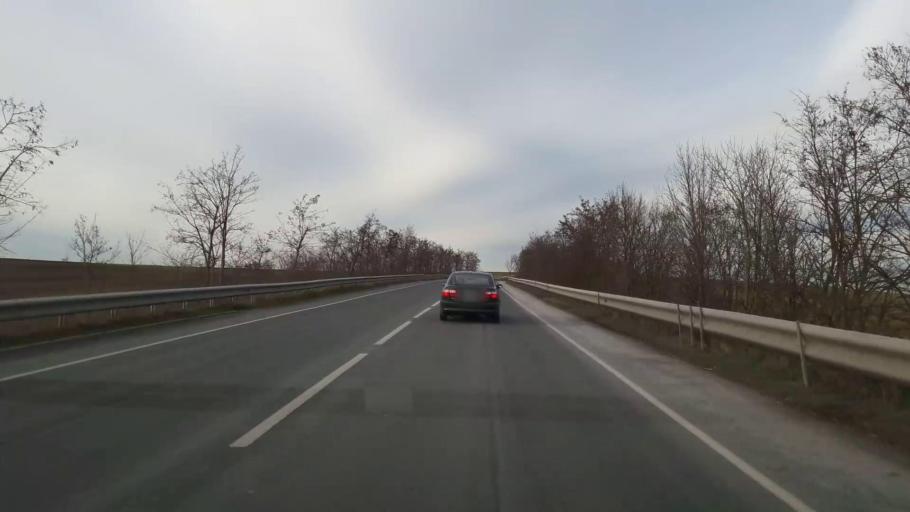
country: AT
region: Lower Austria
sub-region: Politischer Bezirk Mistelbach
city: Drasenhofen
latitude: 48.7308
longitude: 16.6572
